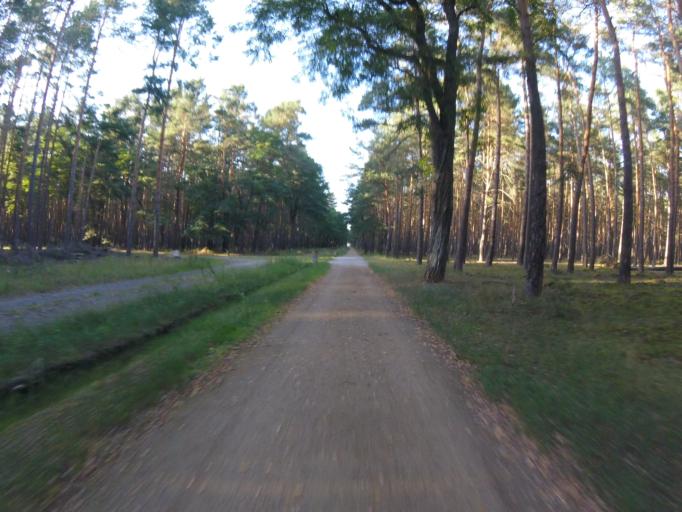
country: DE
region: Brandenburg
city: Munchehofe
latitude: 52.2100
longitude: 13.7708
